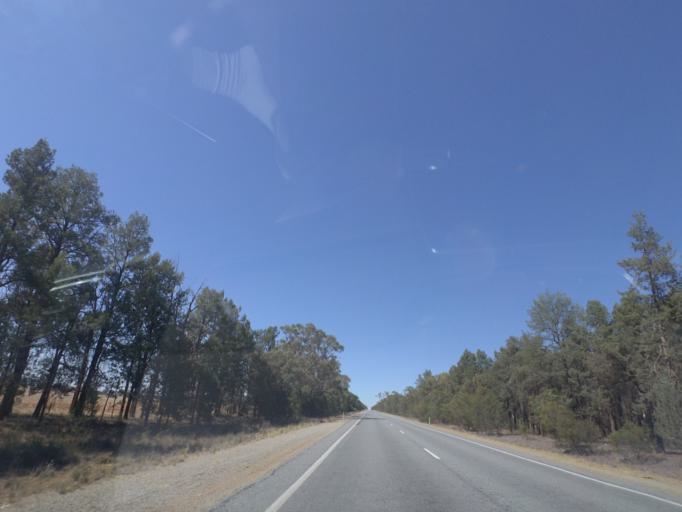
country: AU
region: New South Wales
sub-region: Narrandera
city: Narrandera
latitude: -34.4256
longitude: 146.8442
